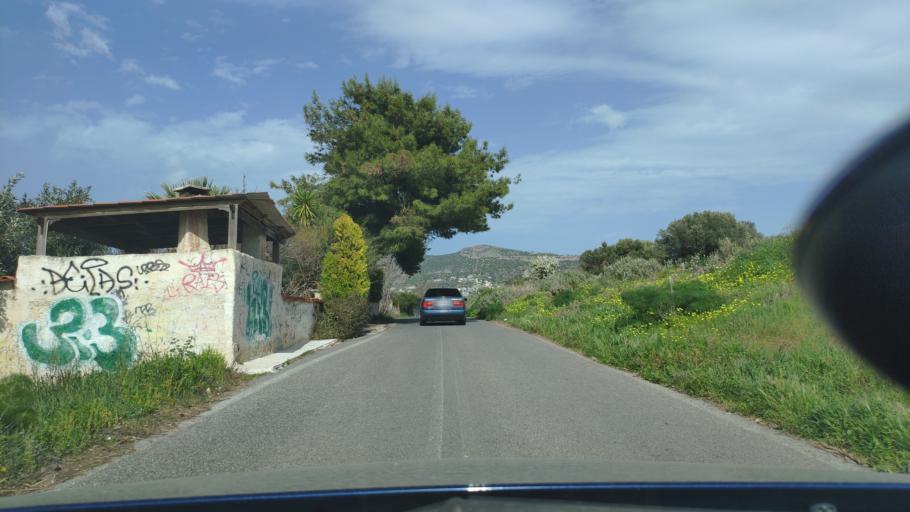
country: GR
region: Attica
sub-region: Nomarchia Anatolikis Attikis
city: Limin Mesoyaias
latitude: 37.8853
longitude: 24.0143
